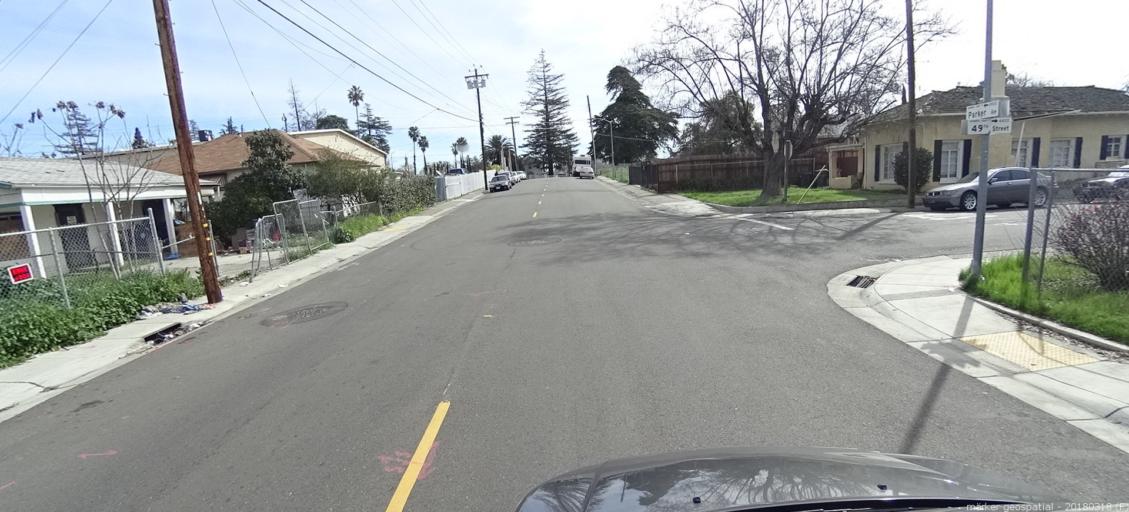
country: US
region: California
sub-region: Sacramento County
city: Parkway
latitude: 38.5352
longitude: -121.4489
